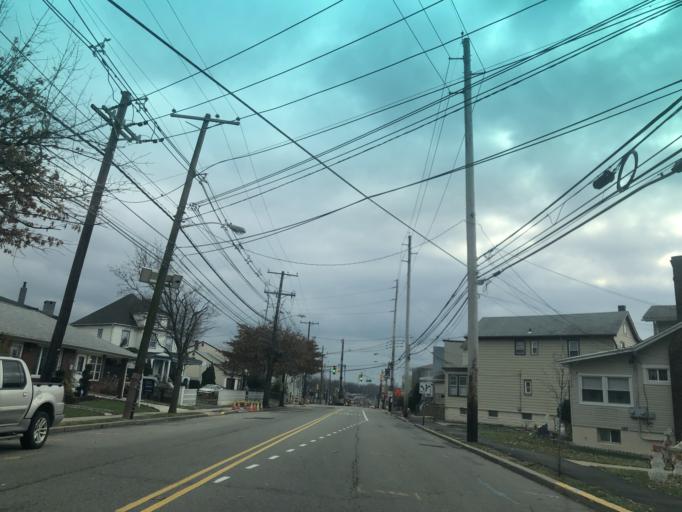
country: US
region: New Jersey
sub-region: Hudson County
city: Secaucus
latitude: 40.7963
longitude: -74.0584
